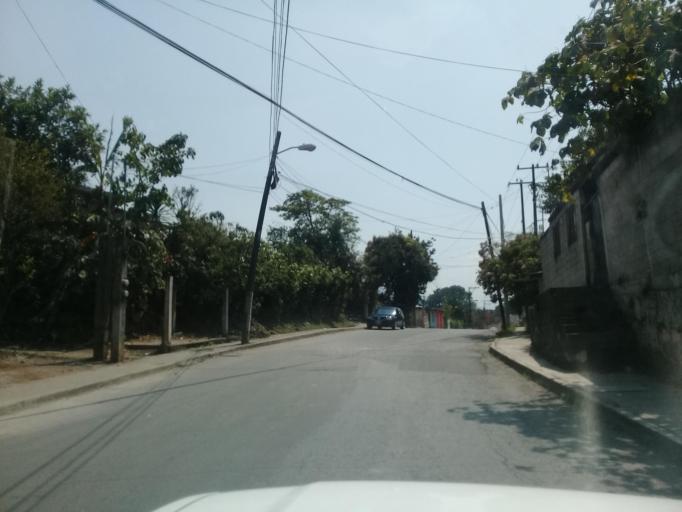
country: MX
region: Veracruz
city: Ixtac Zoquitlan
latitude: 18.8752
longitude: -97.0569
